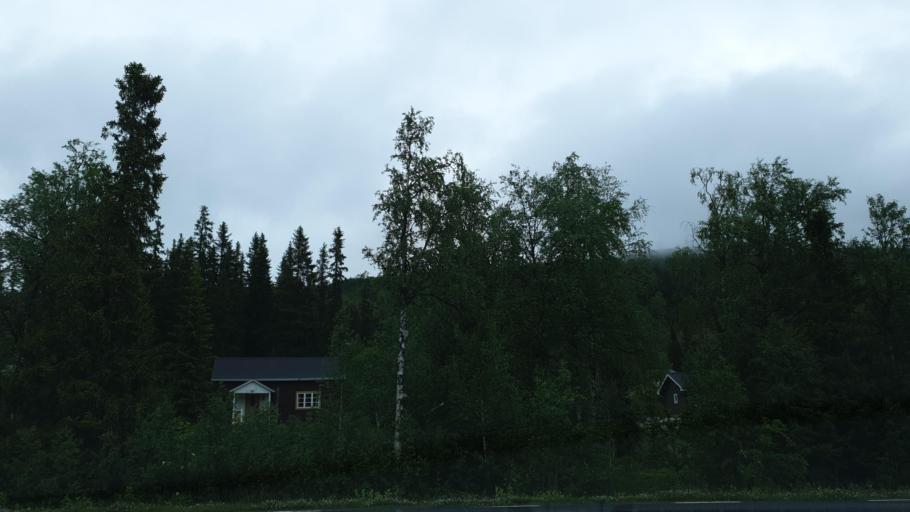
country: SE
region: Vaesterbotten
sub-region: Vilhelmina Kommun
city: Sjoberg
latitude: 65.2517
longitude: 15.5613
